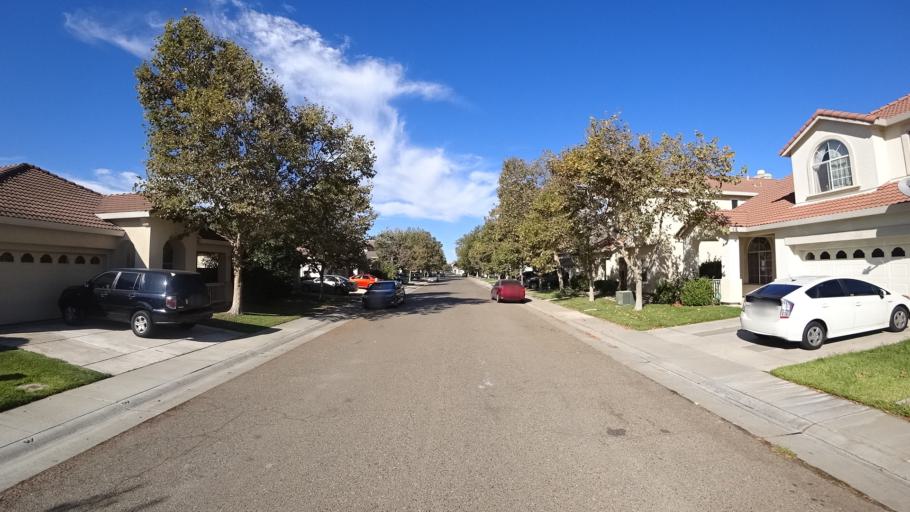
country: US
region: California
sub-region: Sacramento County
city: Laguna
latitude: 38.4171
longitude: -121.4823
